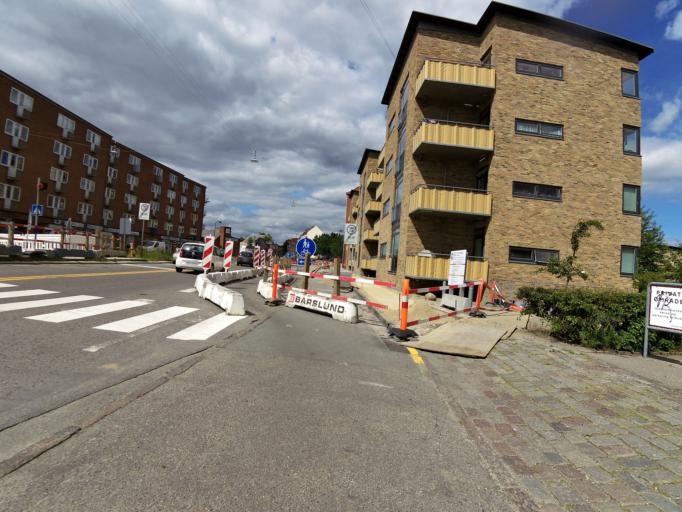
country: DK
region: Capital Region
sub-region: Gladsaxe Municipality
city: Buddinge
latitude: 55.7268
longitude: 12.5256
